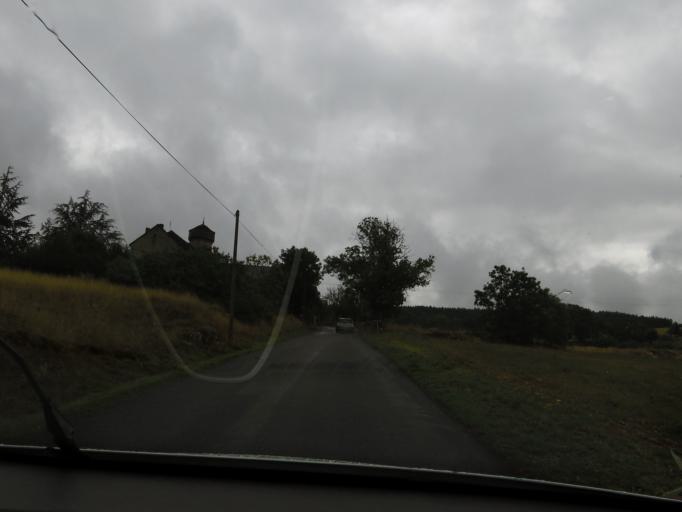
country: FR
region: Languedoc-Roussillon
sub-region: Departement de la Lozere
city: Mende
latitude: 44.4603
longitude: 3.4488
